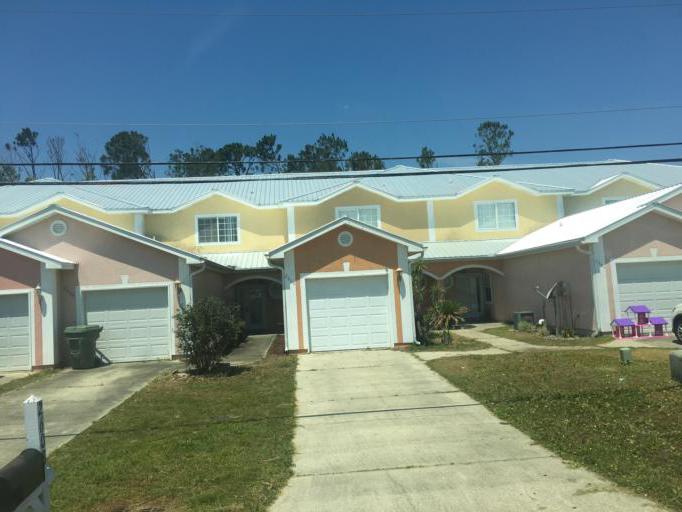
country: US
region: Florida
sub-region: Bay County
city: Lynn Haven
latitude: 30.2184
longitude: -85.6573
